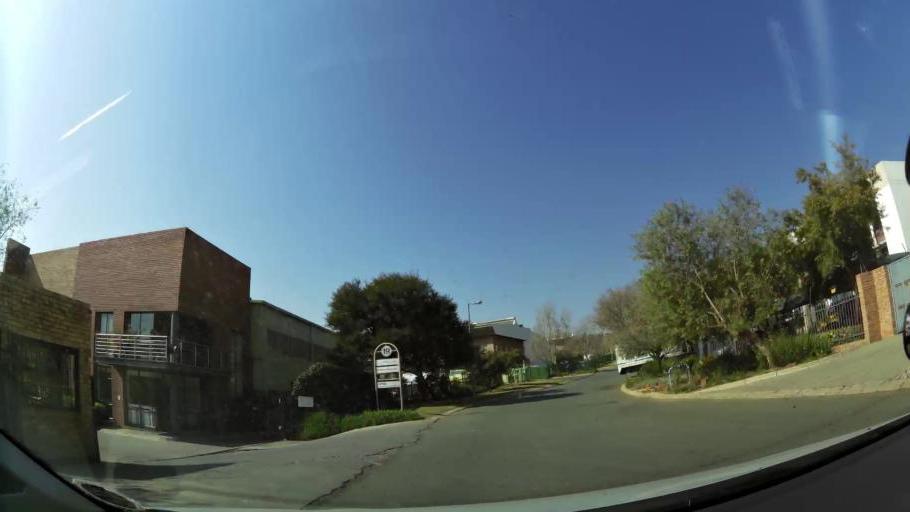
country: ZA
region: Gauteng
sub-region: City of Johannesburg Metropolitan Municipality
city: Modderfontein
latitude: -26.1111
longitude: 28.1396
